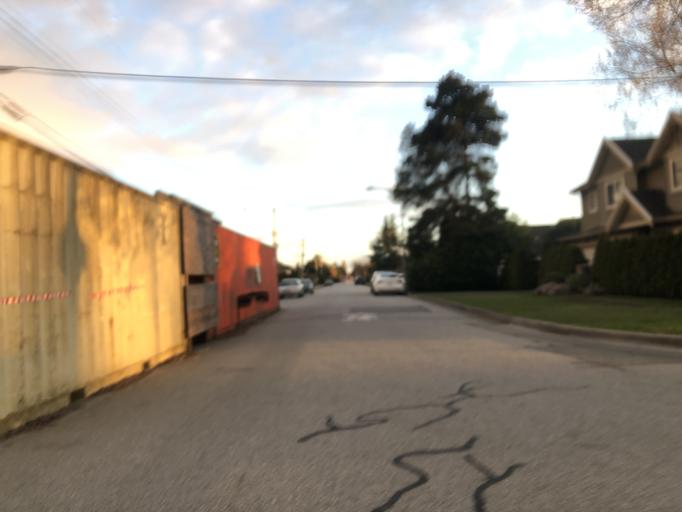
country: CA
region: British Columbia
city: Richmond
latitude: 49.1538
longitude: -123.1197
